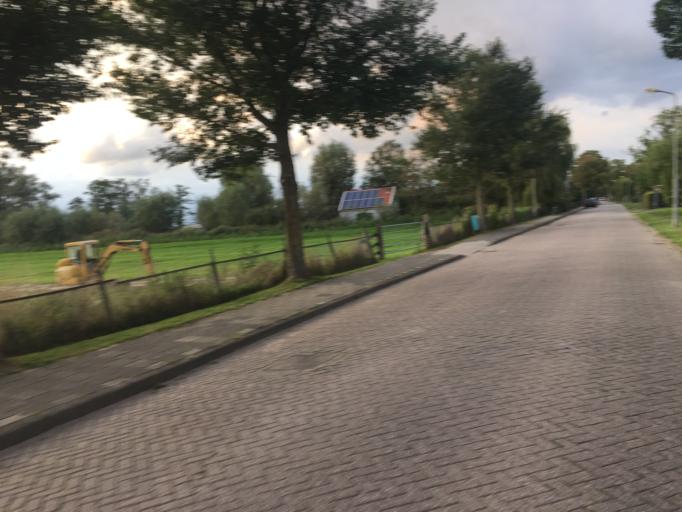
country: NL
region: North Holland
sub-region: Gemeente Zaanstad
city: Zaanstad
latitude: 52.4439
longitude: 4.7775
